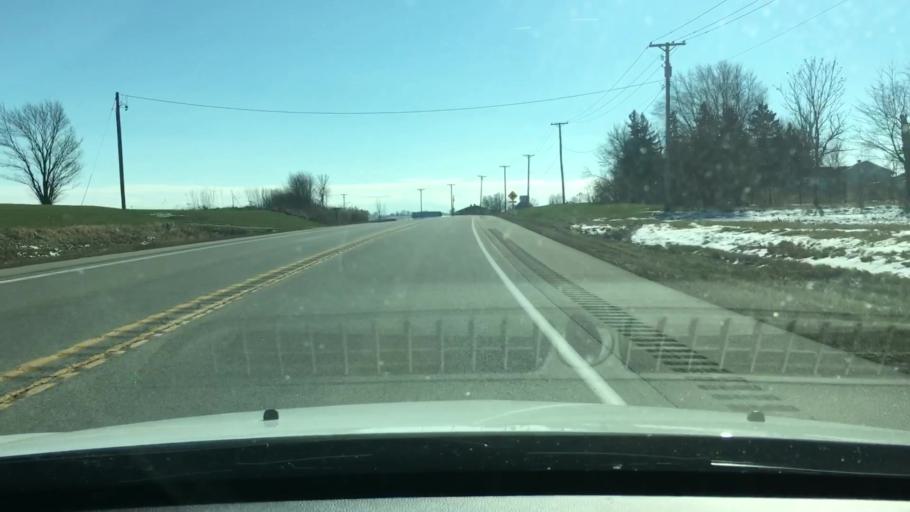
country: US
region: Illinois
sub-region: DeKalb County
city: Malta
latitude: 42.0046
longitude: -88.9371
